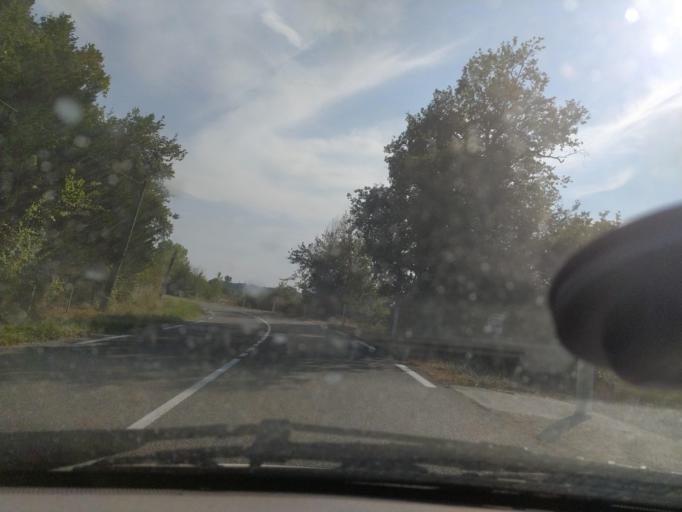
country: FR
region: Midi-Pyrenees
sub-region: Departement du Gers
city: Nogaro
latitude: 43.7773
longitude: -0.0299
